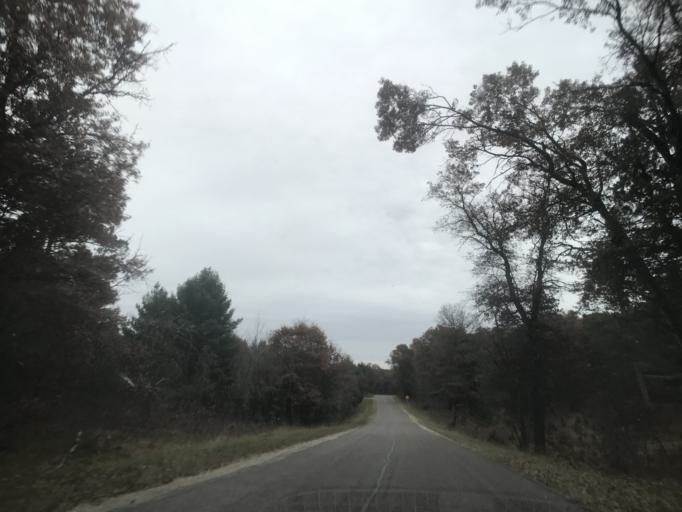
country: US
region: Wisconsin
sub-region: Oconto County
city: Gillett
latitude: 45.2644
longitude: -88.2536
